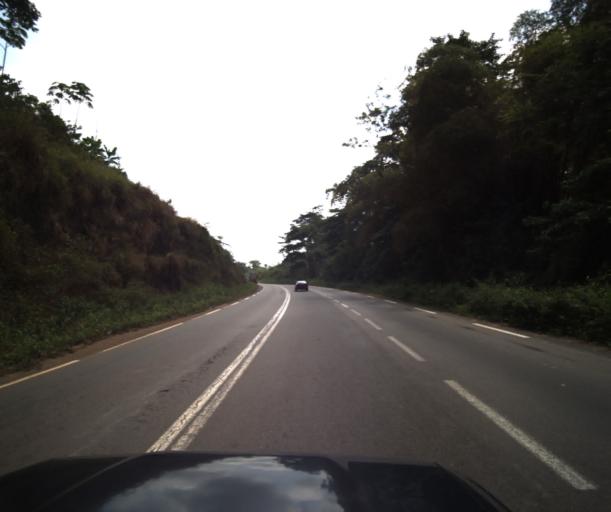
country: CM
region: Centre
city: Eseka
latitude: 3.8718
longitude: 10.8316
